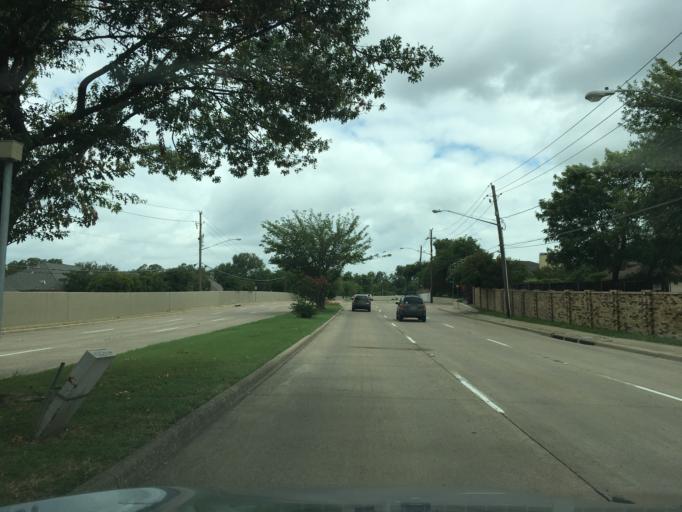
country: US
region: Texas
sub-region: Dallas County
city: Richardson
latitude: 32.8895
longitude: -96.7416
